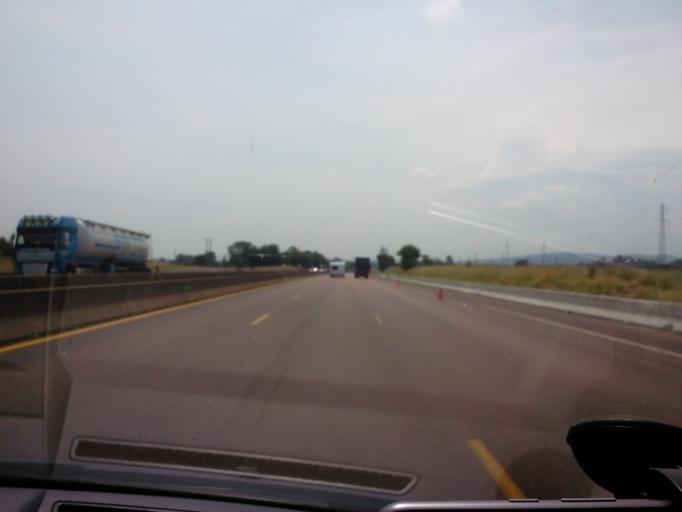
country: FR
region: Bourgogne
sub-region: Departement de Saone-et-Loire
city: Tournus
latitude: 46.5018
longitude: 4.9123
